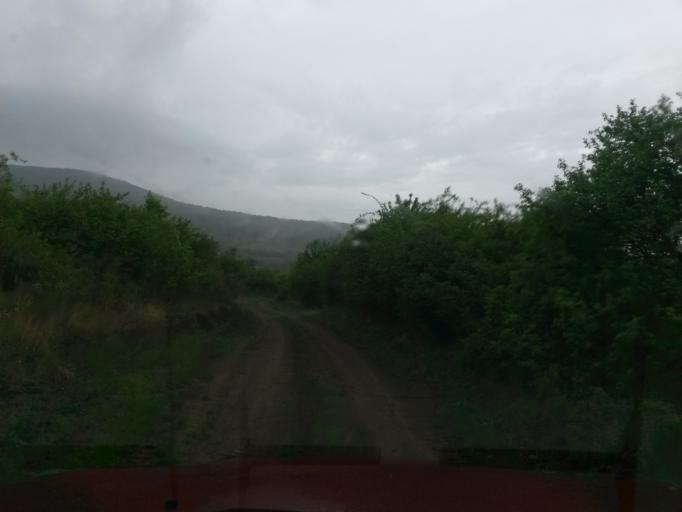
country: HU
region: Borsod-Abauj-Zemplen
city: Gonc
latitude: 48.5116
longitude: 21.3317
